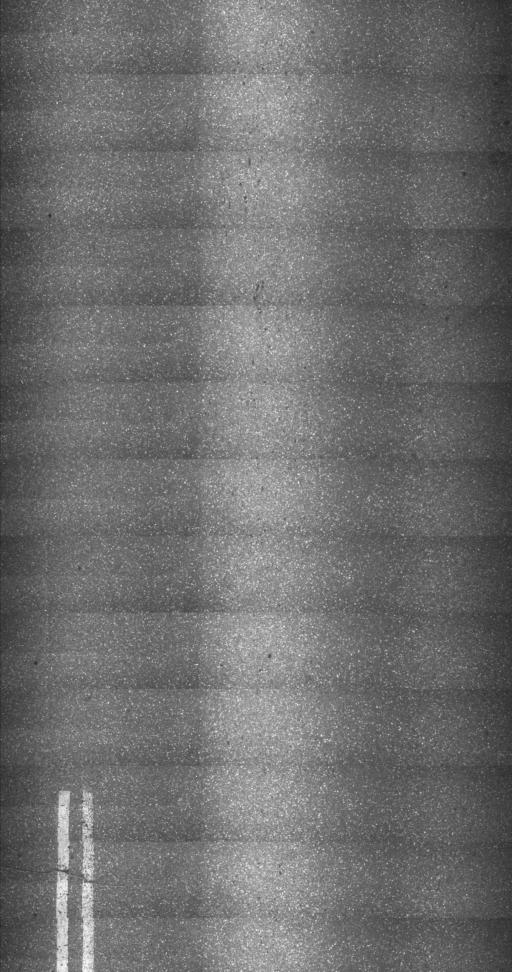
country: US
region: Vermont
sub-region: Washington County
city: Northfield
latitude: 44.1413
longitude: -72.6575
